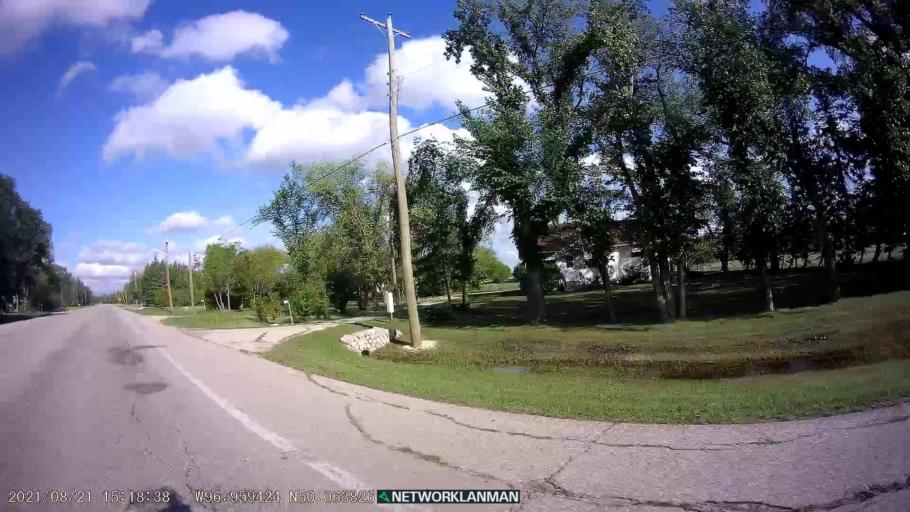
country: CA
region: Manitoba
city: Selkirk
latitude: 50.0639
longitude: -96.9588
